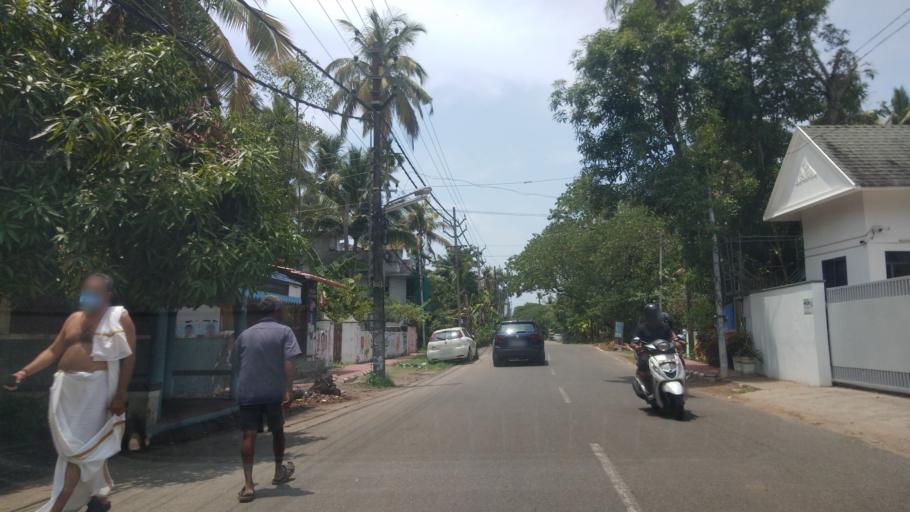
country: IN
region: Kerala
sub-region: Ernakulam
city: Cochin
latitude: 9.8860
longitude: 76.2609
